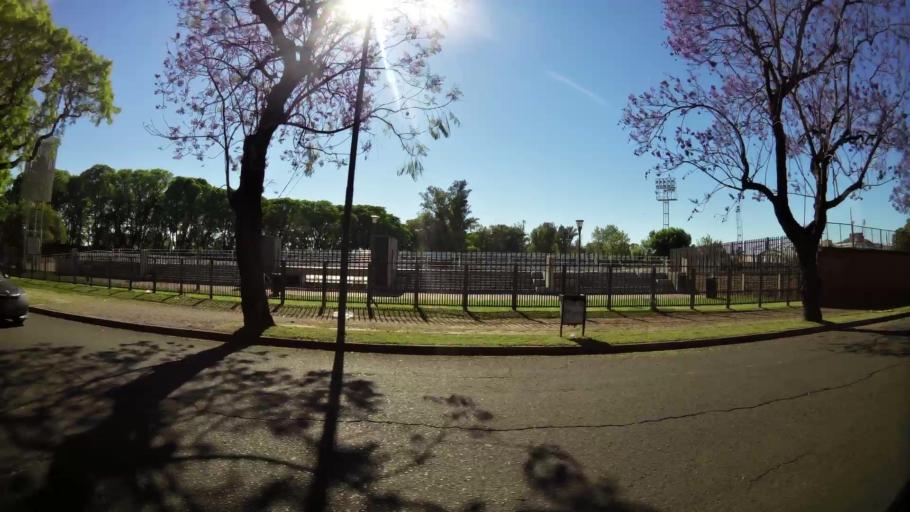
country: AR
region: Santa Fe
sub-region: Departamento de Rosario
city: Rosario
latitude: -32.9611
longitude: -60.6660
